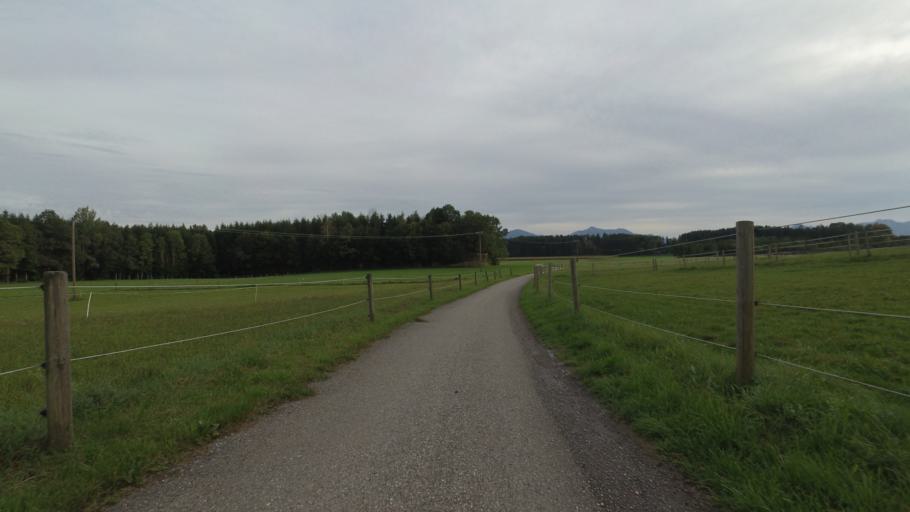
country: DE
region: Bavaria
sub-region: Upper Bavaria
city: Chieming
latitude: 47.9282
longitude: 12.5354
